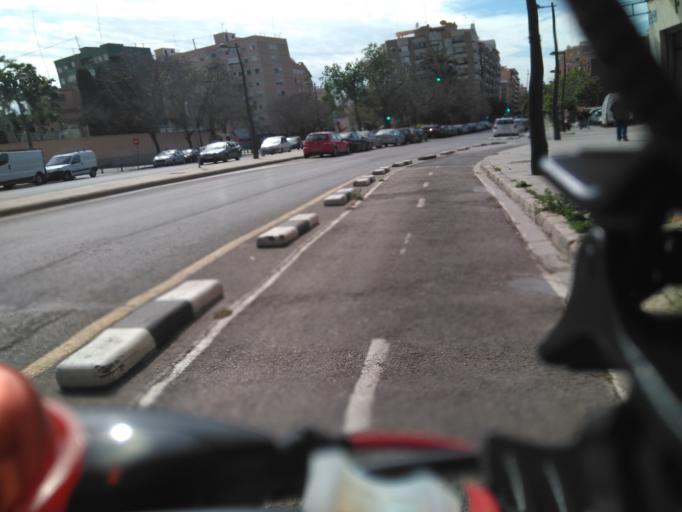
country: ES
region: Valencia
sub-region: Provincia de Valencia
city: Valencia
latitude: 39.4866
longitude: -0.3875
